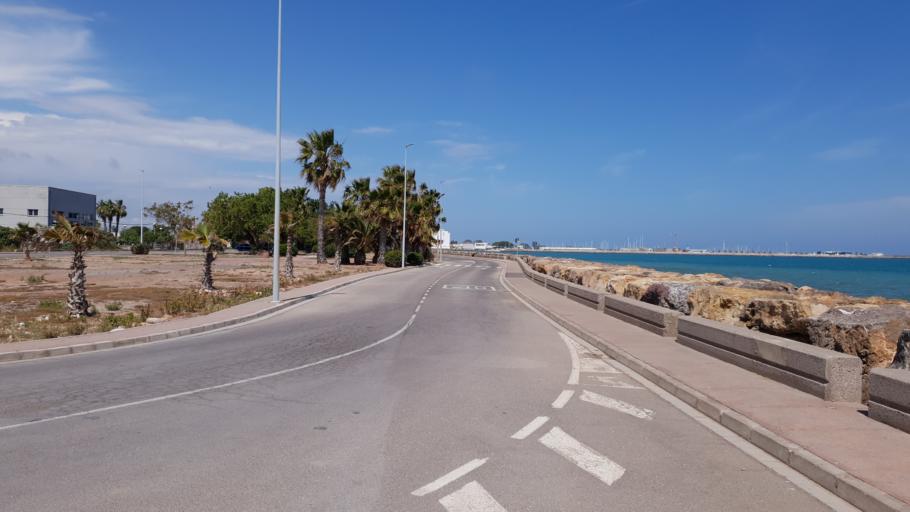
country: ES
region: Valencia
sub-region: Provincia de Castello
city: Burriana
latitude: 39.8573
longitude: -0.0857
